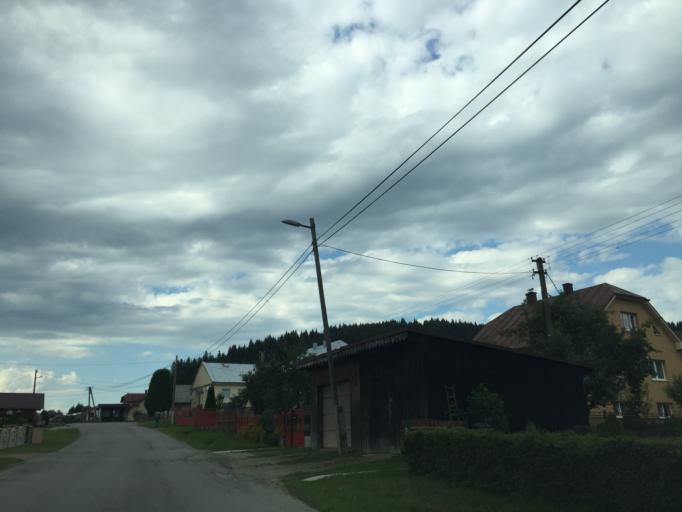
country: PL
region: Silesian Voivodeship
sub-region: Powiat zywiecki
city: Sopotnia Wielka
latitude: 49.4378
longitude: 19.3154
